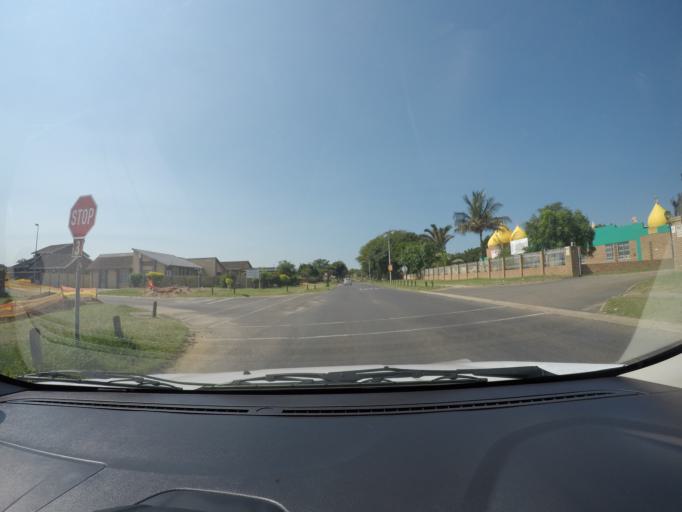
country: ZA
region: KwaZulu-Natal
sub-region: uThungulu District Municipality
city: Richards Bay
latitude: -28.7286
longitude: 32.0416
